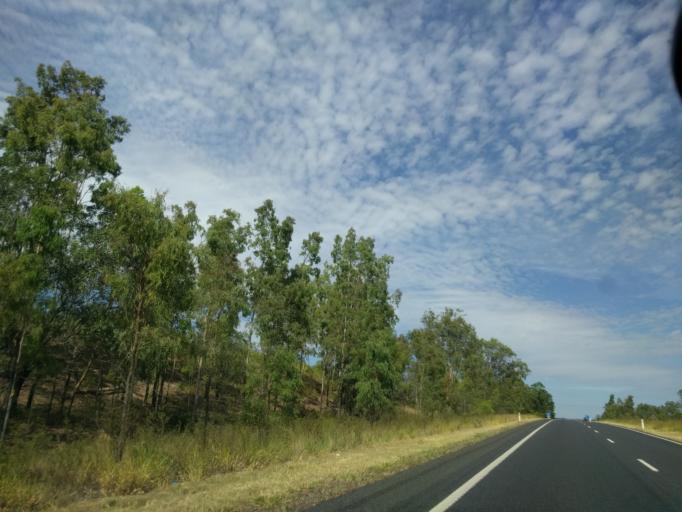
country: AU
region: Queensland
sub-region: Lockyer Valley
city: Gatton
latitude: -27.5362
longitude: 152.2652
